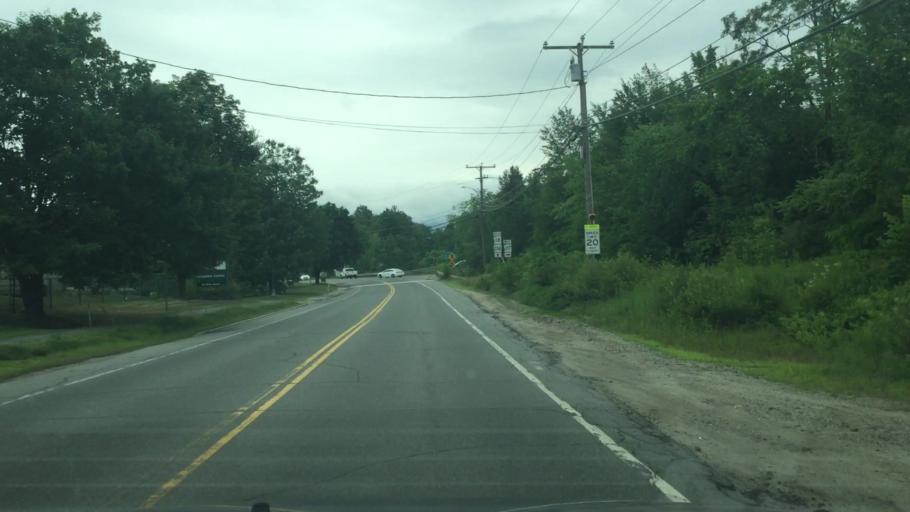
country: US
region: New Hampshire
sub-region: Grafton County
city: Littleton
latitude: 44.2322
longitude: -71.7560
